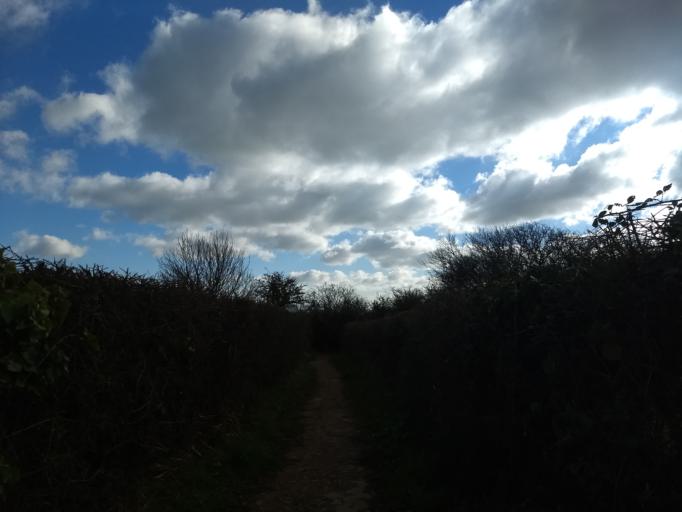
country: GB
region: England
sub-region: Isle of Wight
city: Bembridge
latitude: 50.6784
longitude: -1.0857
